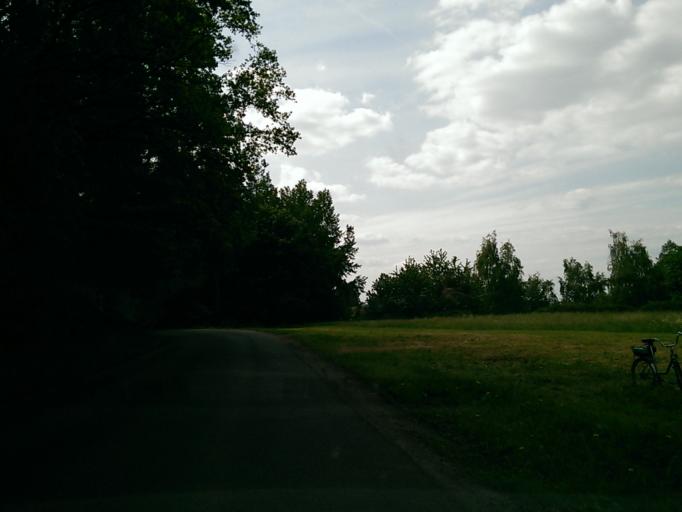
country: CZ
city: Prisovice
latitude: 50.5624
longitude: 15.1129
